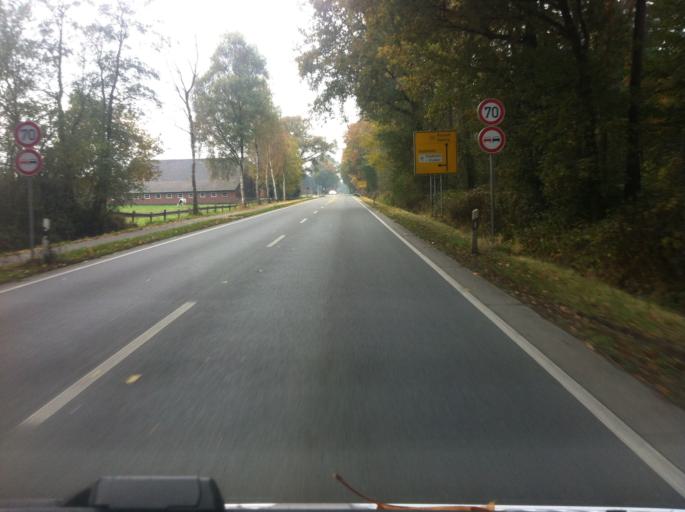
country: DE
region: North Rhine-Westphalia
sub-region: Regierungsbezirk Munster
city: Vreden
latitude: 52.0052
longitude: 6.8240
